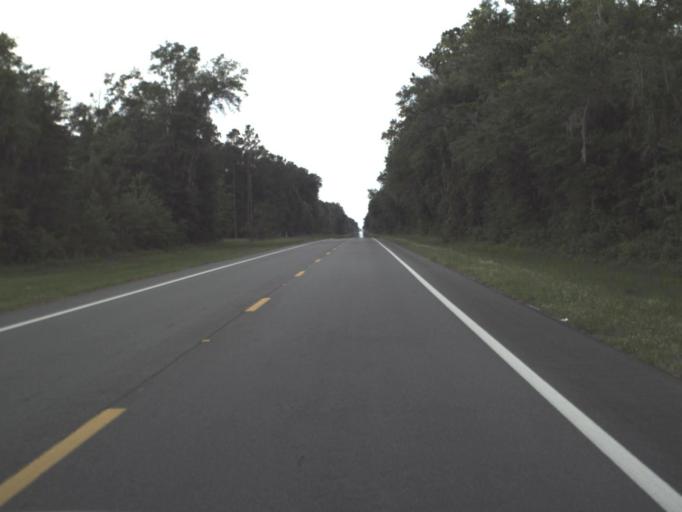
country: US
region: Florida
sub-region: Columbia County
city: Five Points
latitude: 30.4457
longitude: -82.6471
